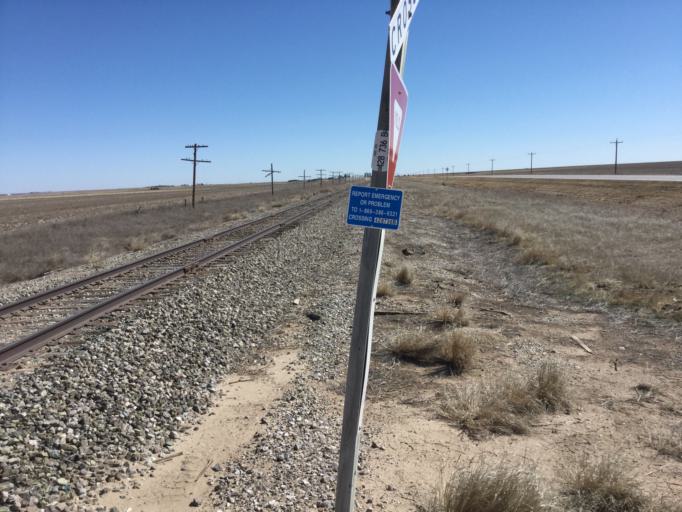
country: US
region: Kansas
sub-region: Greeley County
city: Tribune
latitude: 38.4640
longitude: -101.6043
